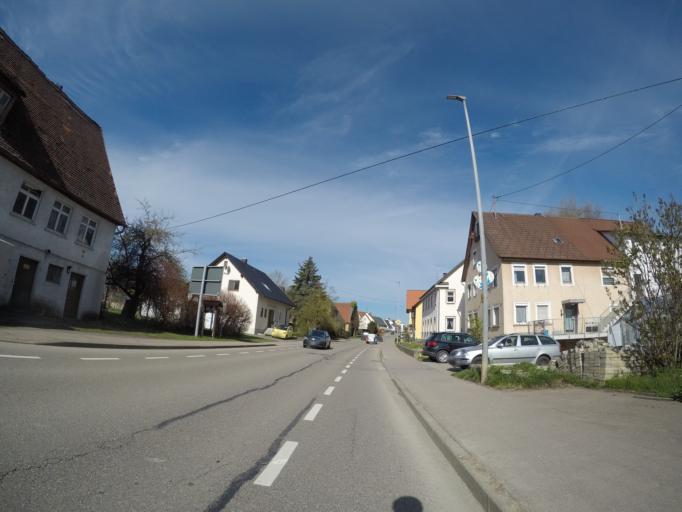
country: DE
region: Baden-Wuerttemberg
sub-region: Tuebingen Region
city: Laichingen
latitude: 48.4930
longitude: 9.6848
